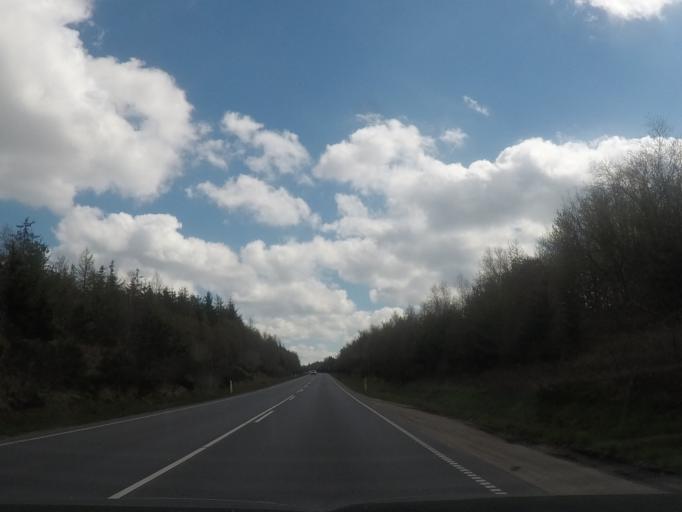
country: DK
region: South Denmark
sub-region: Kolding Kommune
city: Kolding
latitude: 55.5504
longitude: 9.4914
